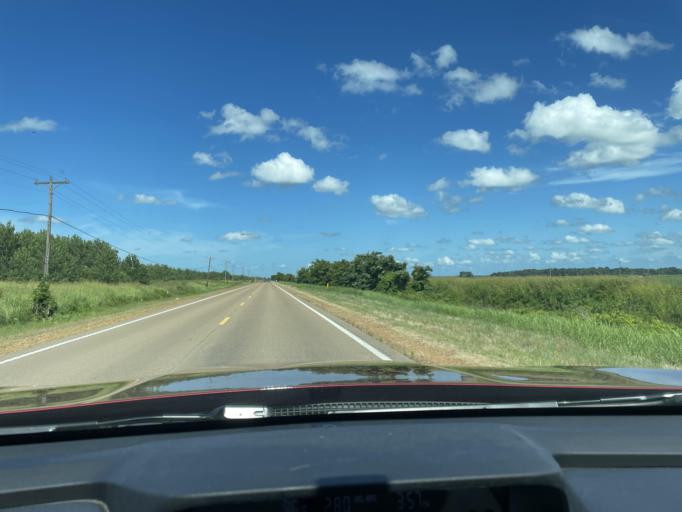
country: US
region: Mississippi
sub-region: Humphreys County
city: Belzoni
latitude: 33.1830
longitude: -90.6143
